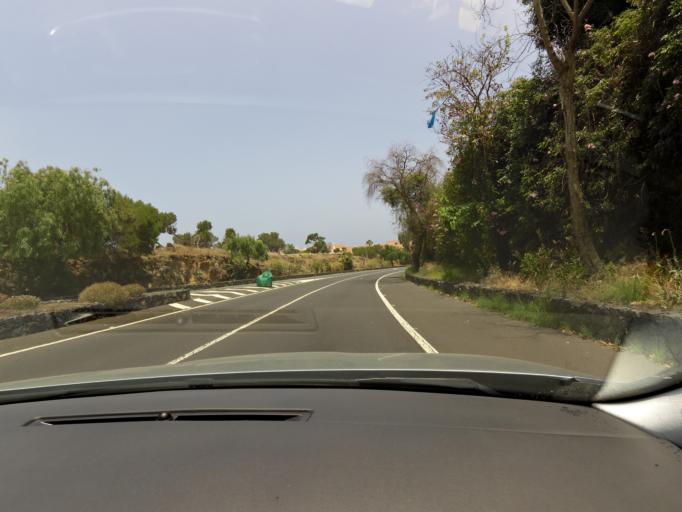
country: ES
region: Canary Islands
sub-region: Provincia de Santa Cruz de Tenerife
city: Puerto de la Cruz
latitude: 28.4085
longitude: -16.5329
